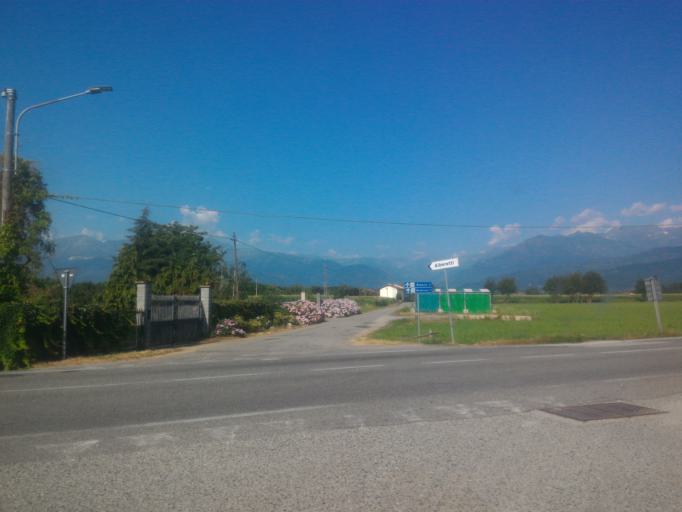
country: IT
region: Piedmont
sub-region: Provincia di Torino
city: Garzigliana
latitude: 44.8327
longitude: 7.3644
